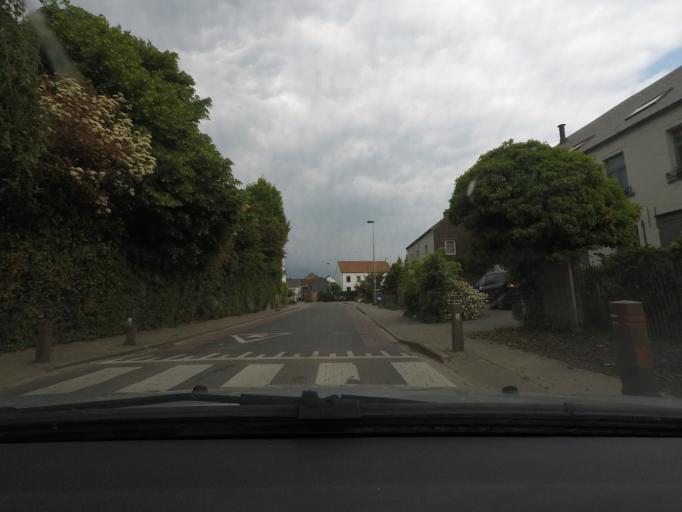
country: BE
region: Wallonia
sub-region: Province du Hainaut
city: Basse Lasne
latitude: 50.6599
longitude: 4.5150
